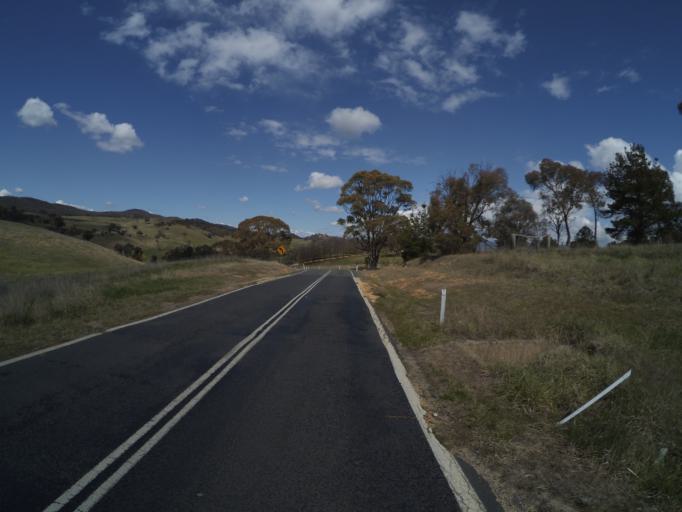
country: AU
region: Australian Capital Territory
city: Macquarie
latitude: -35.3814
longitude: 148.9624
